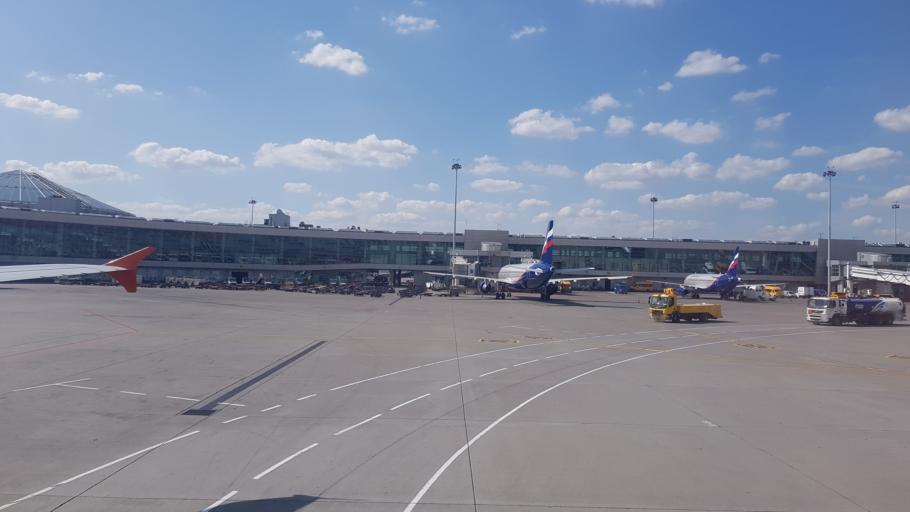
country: RU
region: Moskovskaya
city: Novopodrezkovo
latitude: 55.9645
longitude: 37.4085
